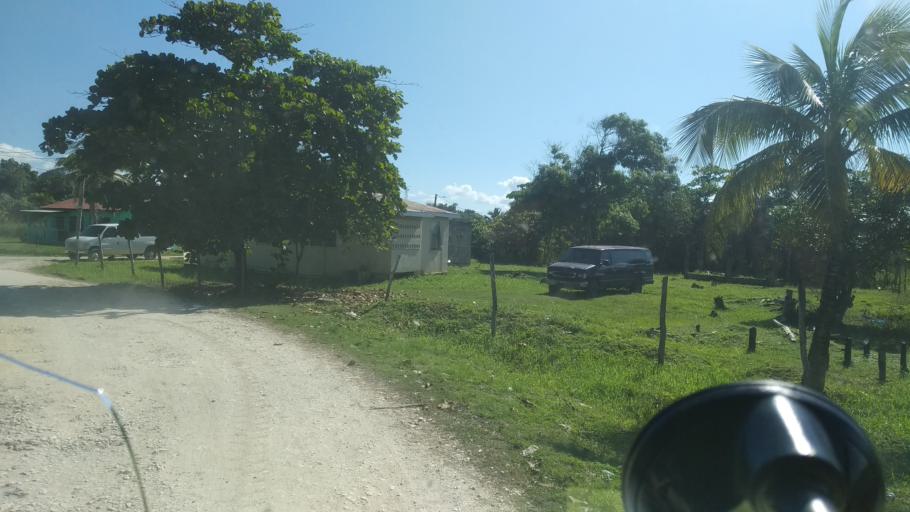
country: BZ
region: Belize
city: Belize City
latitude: 17.5549
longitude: -88.3059
